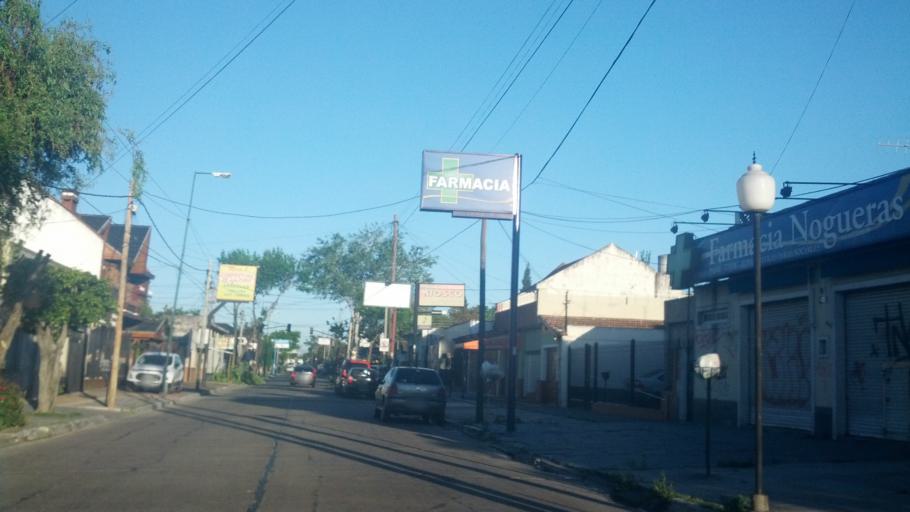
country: AR
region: Buenos Aires
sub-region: Partido de Lomas de Zamora
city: Lomas de Zamora
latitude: -34.7662
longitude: -58.4217
